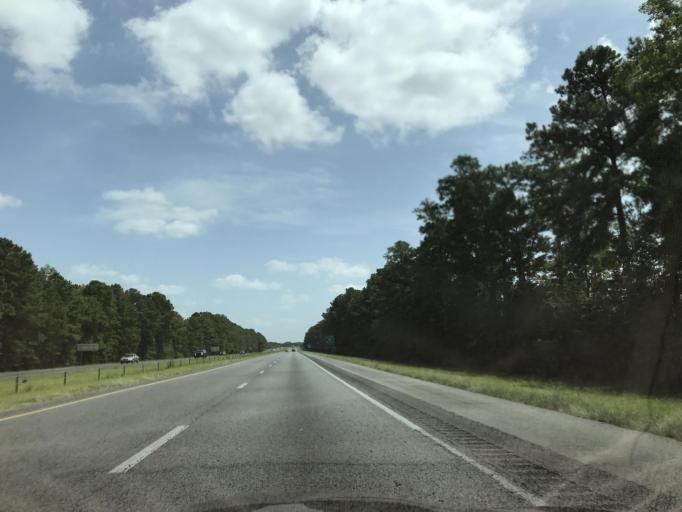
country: US
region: North Carolina
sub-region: Duplin County
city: Wallace
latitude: 34.7645
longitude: -77.9602
